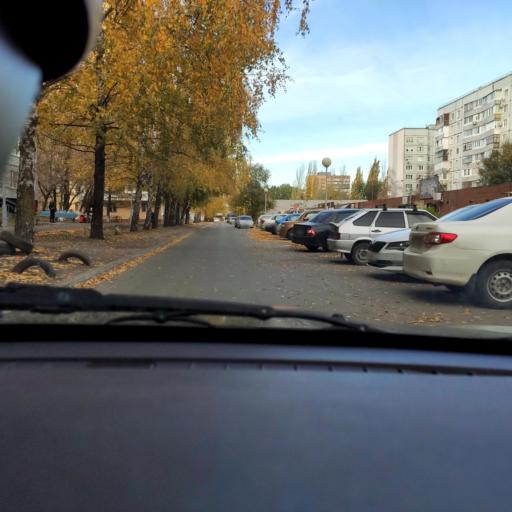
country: RU
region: Samara
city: Tol'yatti
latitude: 53.5077
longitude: 49.2955
